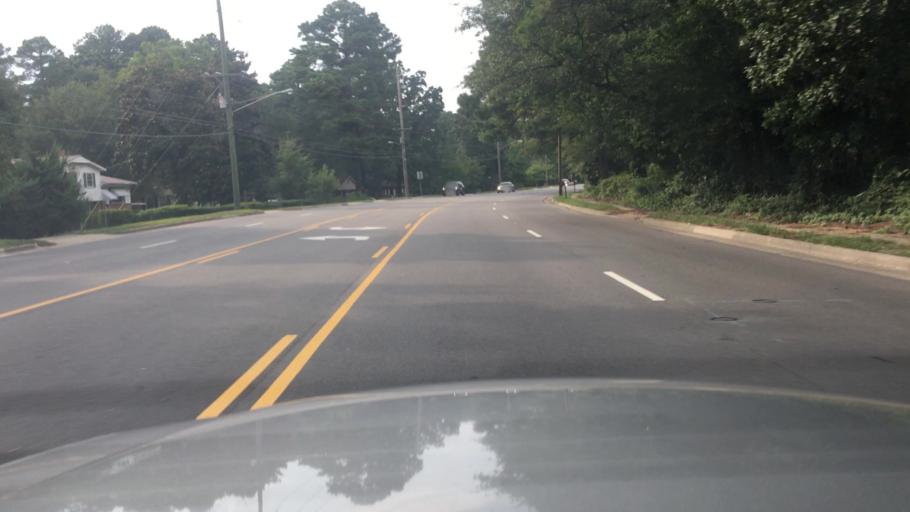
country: US
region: North Carolina
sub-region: Cumberland County
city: Fayetteville
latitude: 35.0611
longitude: -78.9493
